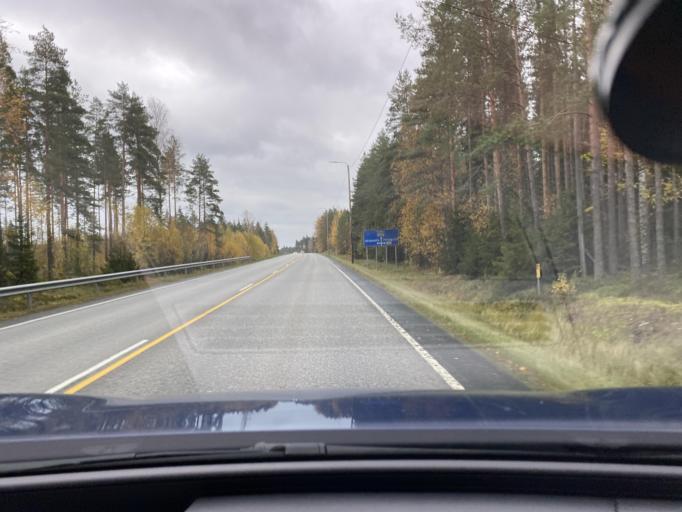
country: FI
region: Varsinais-Suomi
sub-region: Vakka-Suomi
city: Laitila
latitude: 60.9623
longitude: 21.5946
